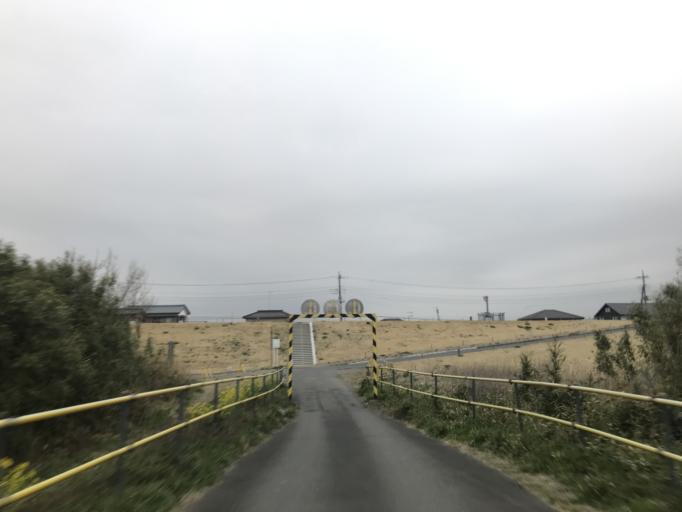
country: JP
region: Ibaraki
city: Mitsukaido
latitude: 36.0300
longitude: 140.0245
